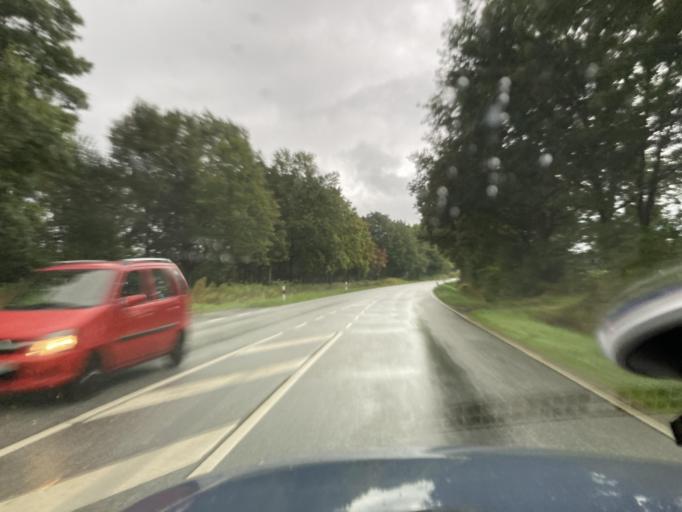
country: DE
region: Schleswig-Holstein
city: Tellingstedt
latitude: 54.2118
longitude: 9.2710
